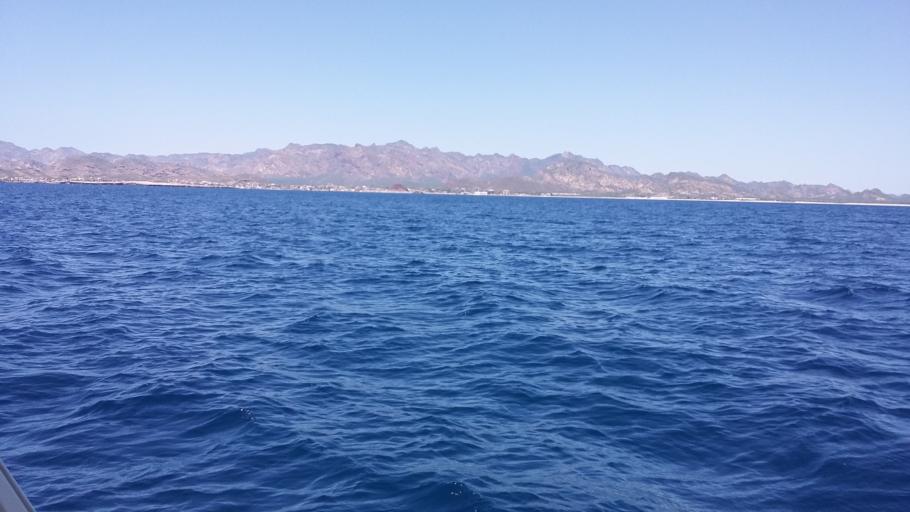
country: MX
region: Sonora
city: Heroica Guaymas
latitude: 27.9271
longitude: -111.0062
